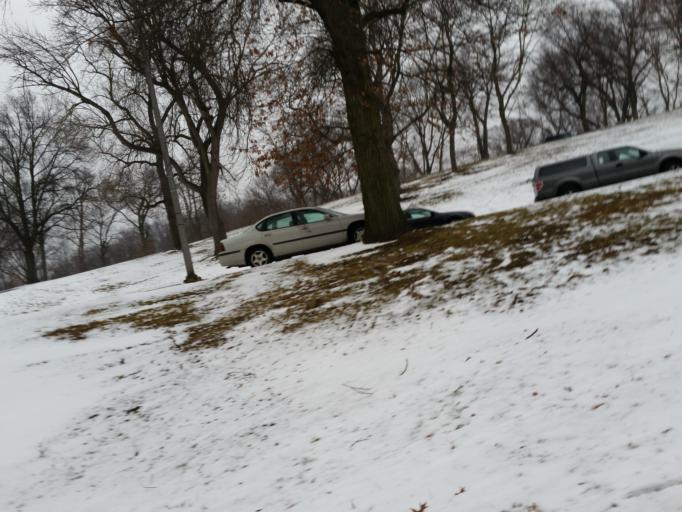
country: US
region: Pennsylvania
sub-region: Allegheny County
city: Bloomfield
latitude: 40.4346
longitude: -79.9455
